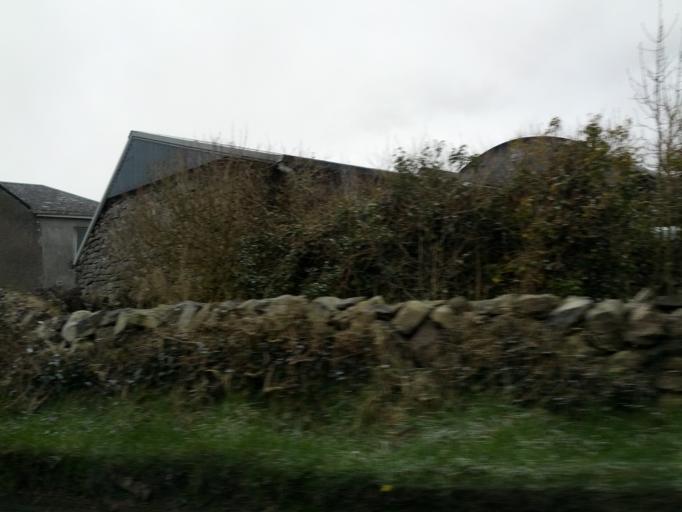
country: IE
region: Connaught
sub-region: County Galway
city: Oranmore
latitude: 53.2404
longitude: -8.8628
